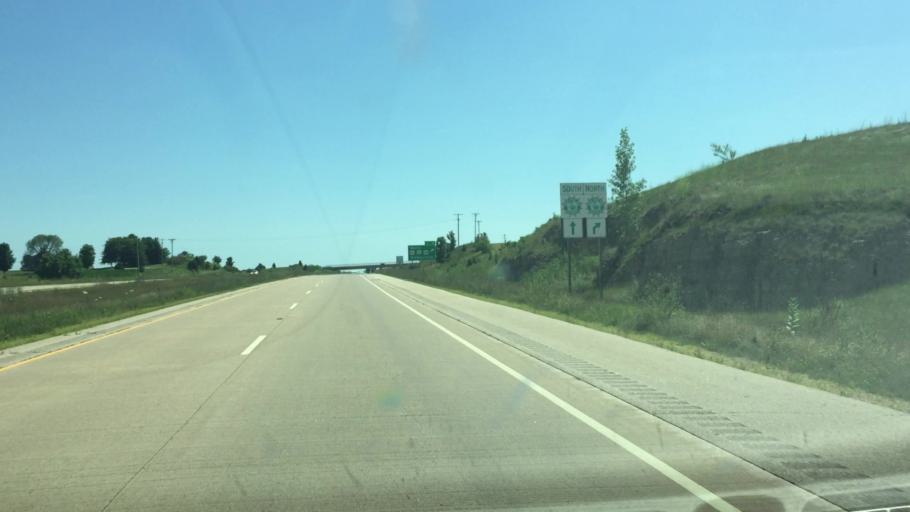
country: US
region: Wisconsin
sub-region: Grant County
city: Dickeyville
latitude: 42.6232
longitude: -90.5832
